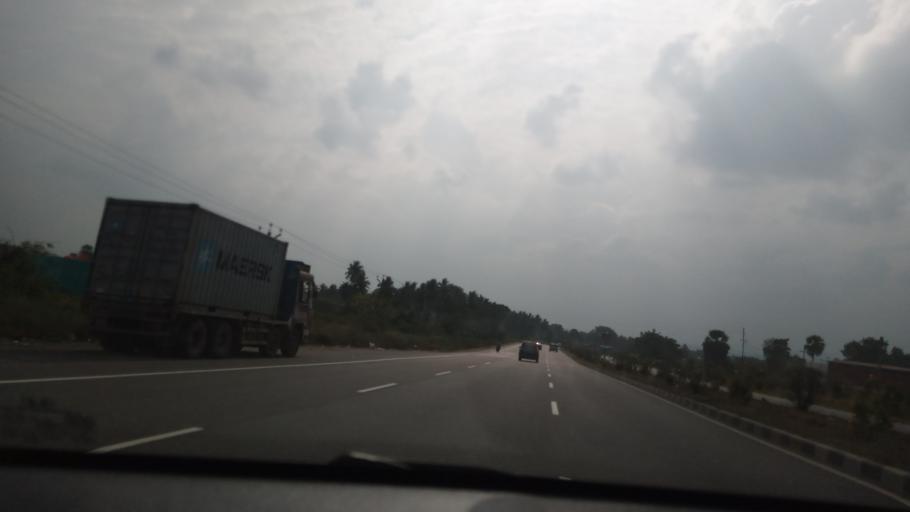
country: IN
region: Tamil Nadu
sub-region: Vellore
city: Vaniyambadi
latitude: 12.6537
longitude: 78.6028
